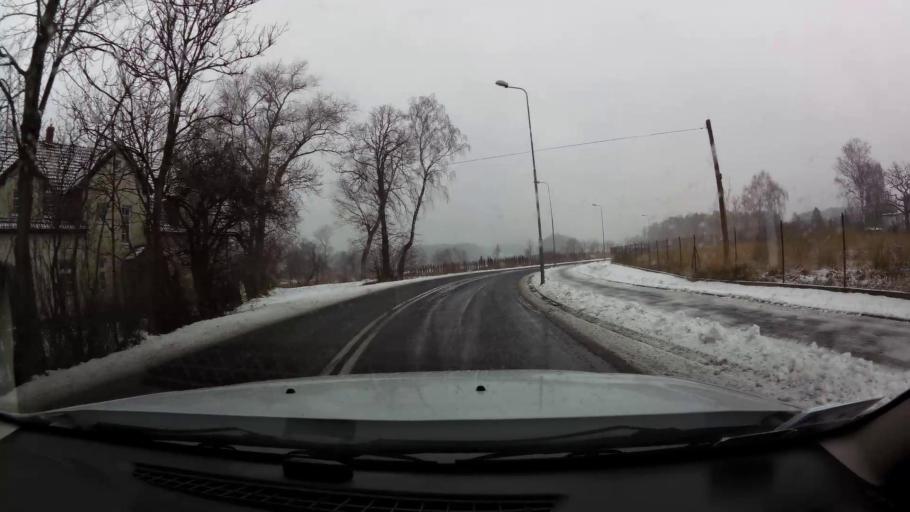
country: PL
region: West Pomeranian Voivodeship
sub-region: Powiat gryficki
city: Mrzezyno
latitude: 54.1354
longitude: 15.2843
